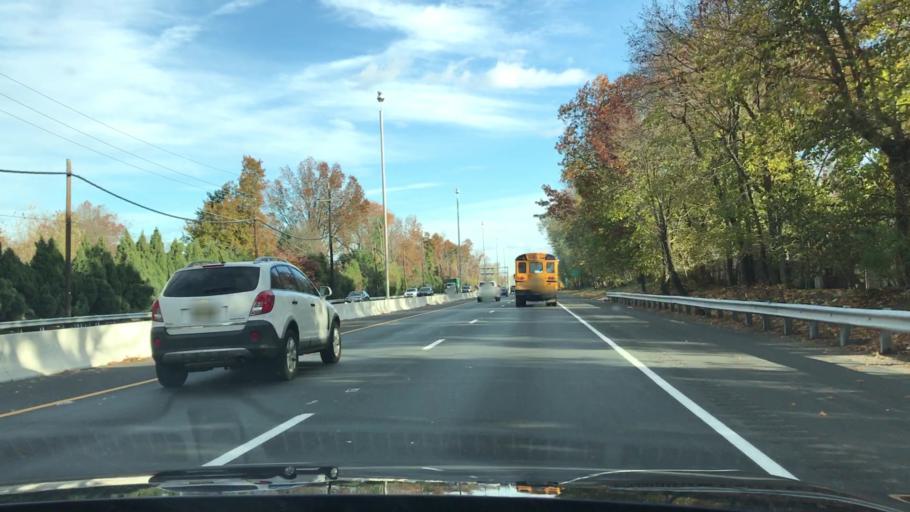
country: US
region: New Jersey
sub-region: Bergen County
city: Elmwood Park
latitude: 40.9296
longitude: -74.1036
